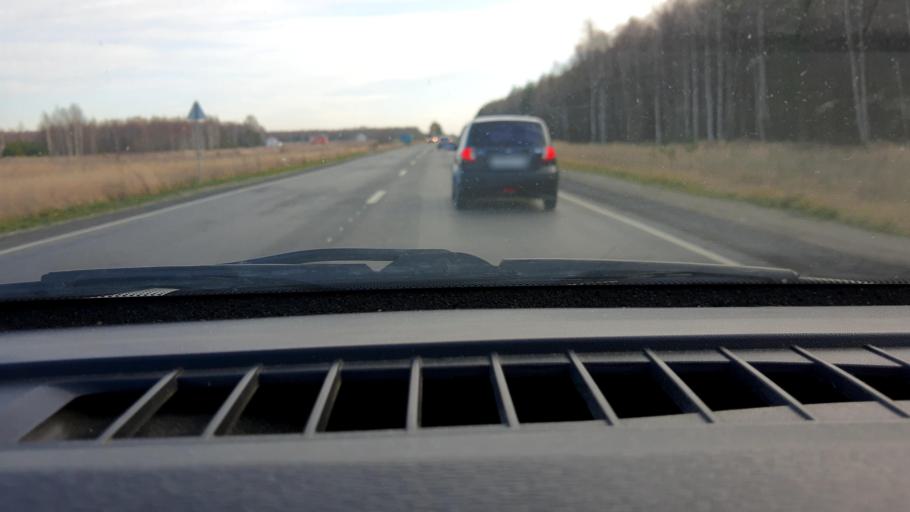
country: RU
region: Nizjnij Novgorod
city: Novaya Balakhna
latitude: 56.6103
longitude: 43.6045
